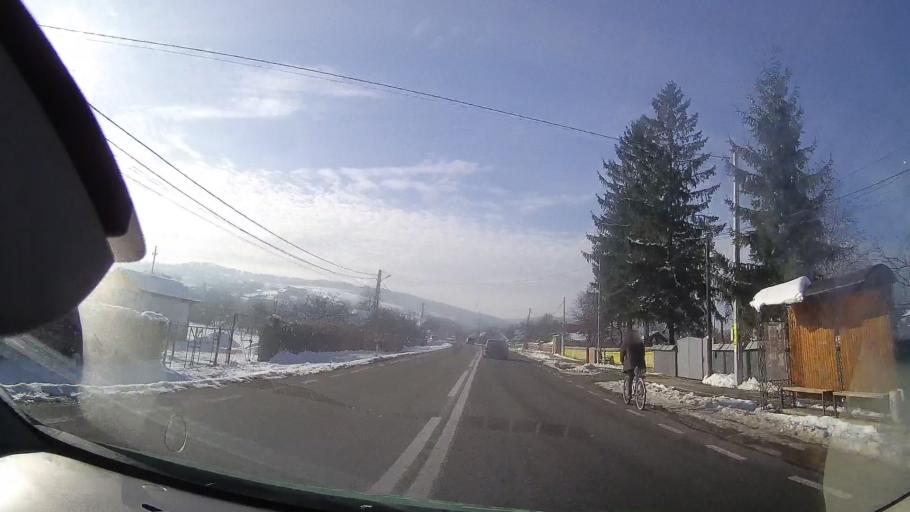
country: RO
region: Neamt
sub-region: Comuna Dobreni
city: Dobreni
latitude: 46.9957
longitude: 26.3956
